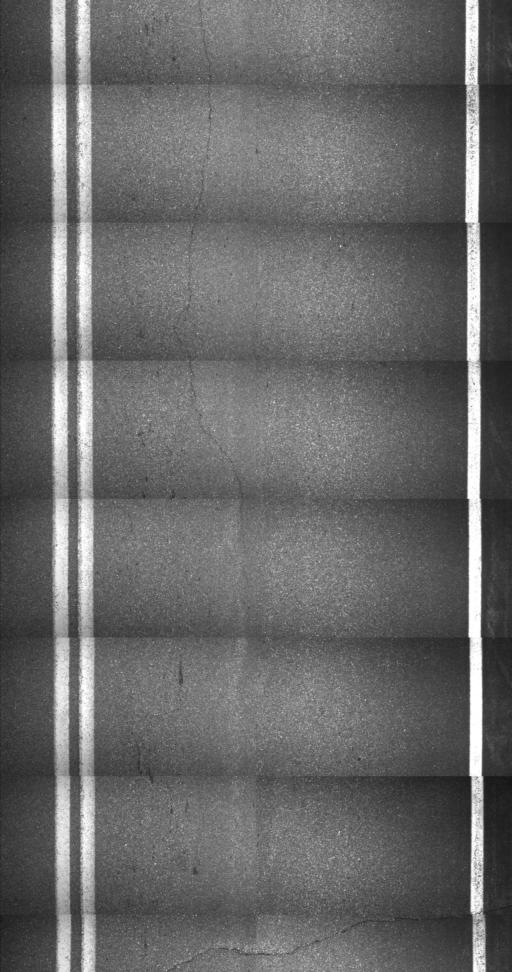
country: US
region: New Hampshire
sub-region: Sullivan County
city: Charlestown
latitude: 43.2287
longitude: -72.4373
